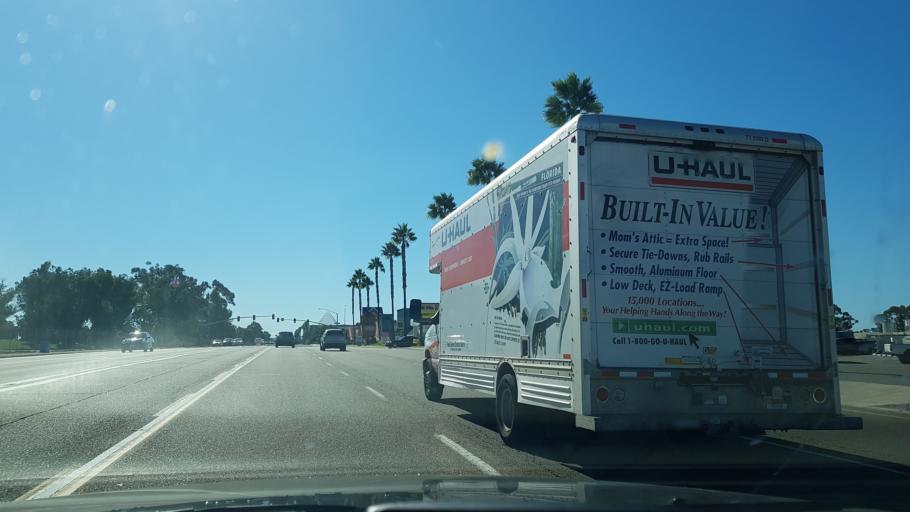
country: US
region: California
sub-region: San Diego County
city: Fairbanks Ranch
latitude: 32.8873
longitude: -117.1472
